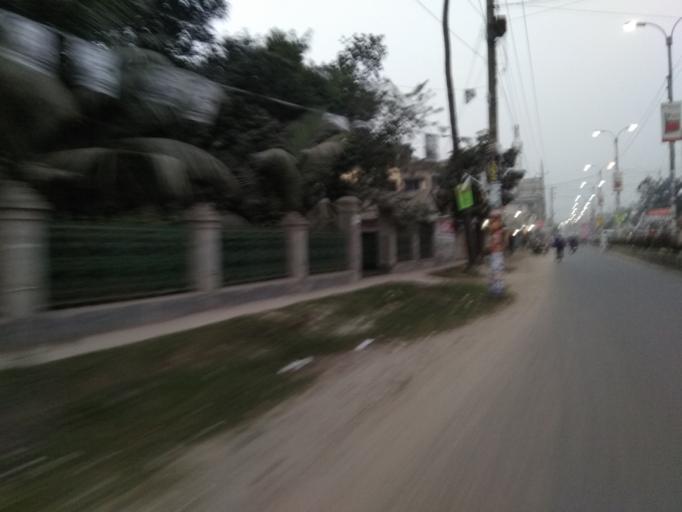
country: BD
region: Rangpur Division
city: Rangpur
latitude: 25.7359
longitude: 89.2547
